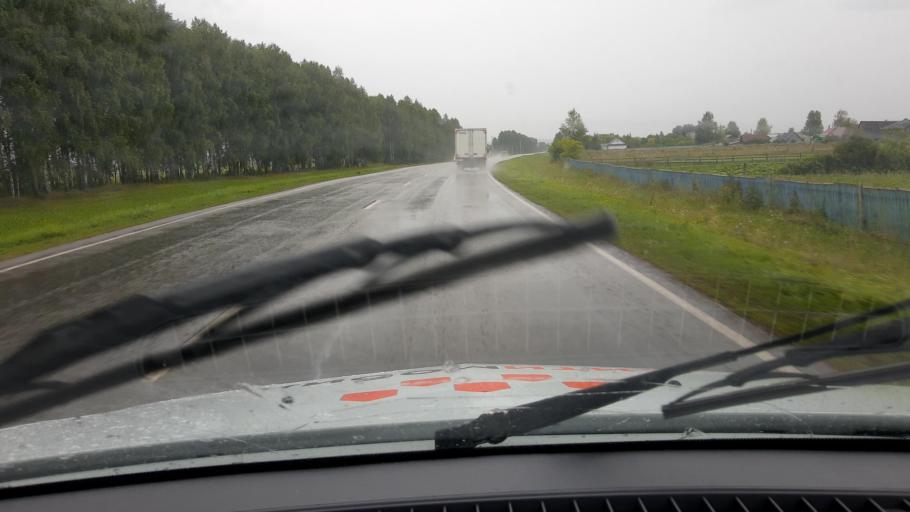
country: RU
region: Bashkortostan
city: Krasnaya Gorka
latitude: 55.0979
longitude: 56.6234
